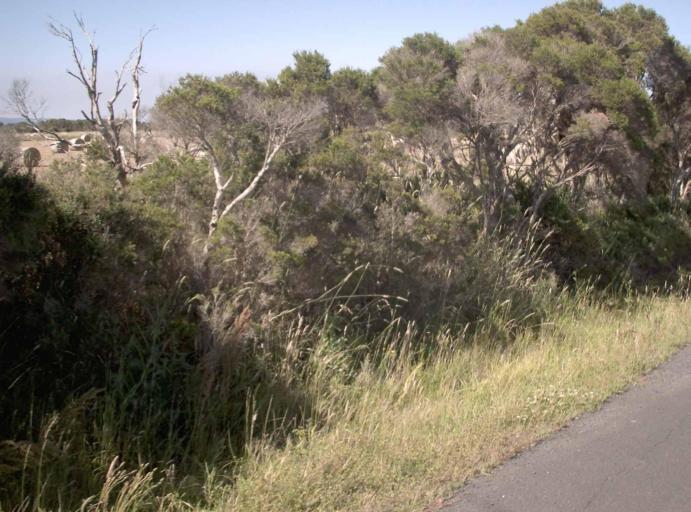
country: AU
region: Victoria
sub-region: Latrobe
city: Traralgon
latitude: -38.6270
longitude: 146.6238
